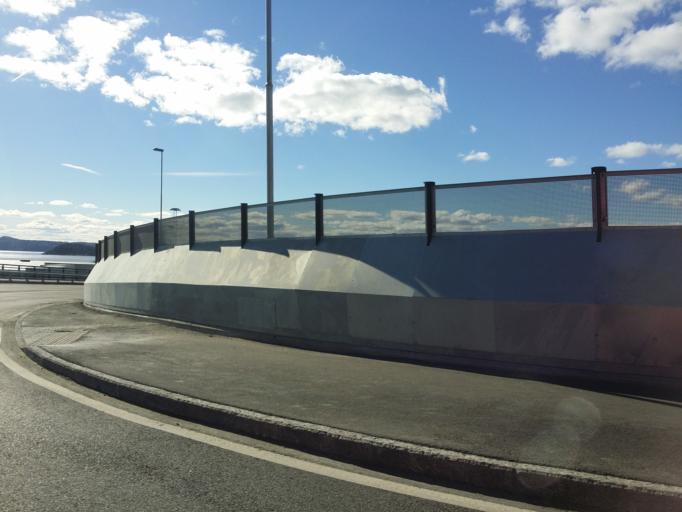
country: NO
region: Oslo
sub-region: Oslo
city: Oslo
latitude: 59.8946
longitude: 10.7578
